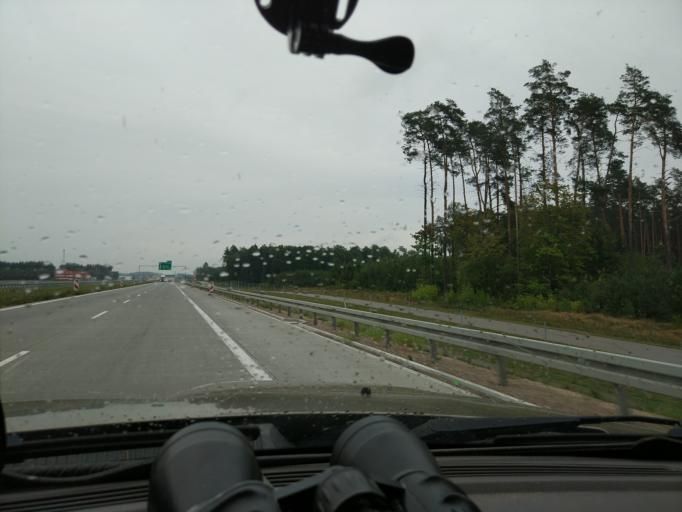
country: PL
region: Masovian Voivodeship
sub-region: Powiat ostrowski
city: Brok
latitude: 52.7508
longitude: 21.7814
